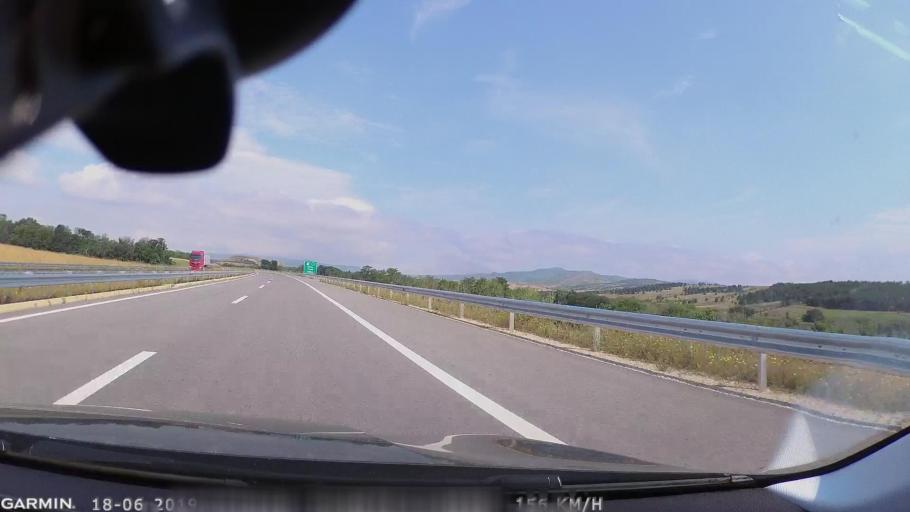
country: MK
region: Sveti Nikole
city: Gorobinci
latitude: 41.9089
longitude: 21.9039
